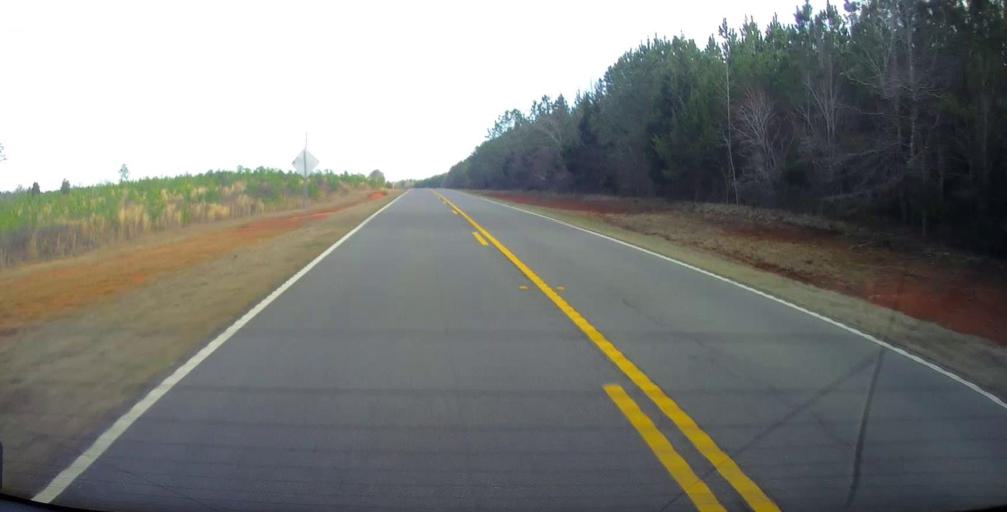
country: US
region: Georgia
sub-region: Harris County
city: Hamilton
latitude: 32.6934
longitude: -84.7949
